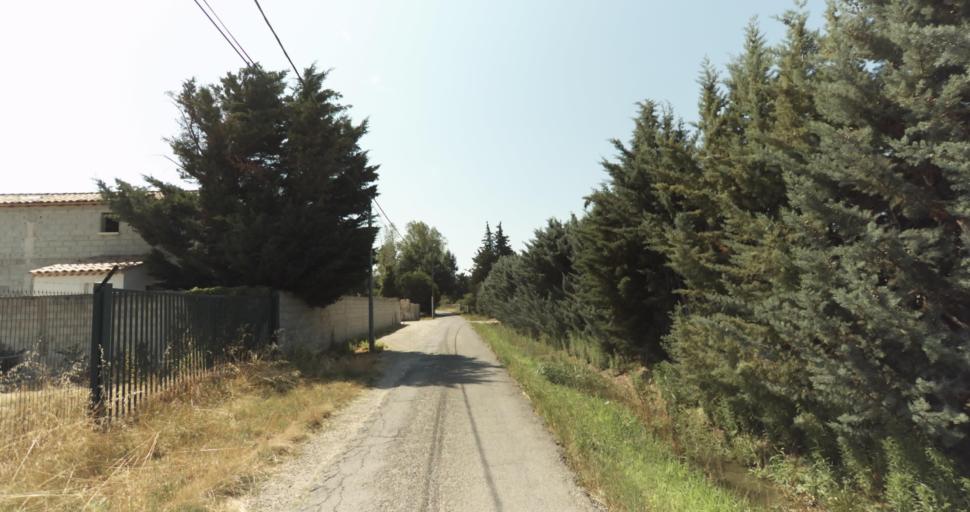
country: FR
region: Provence-Alpes-Cote d'Azur
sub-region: Departement du Vaucluse
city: Monteux
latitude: 44.0233
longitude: 5.0100
